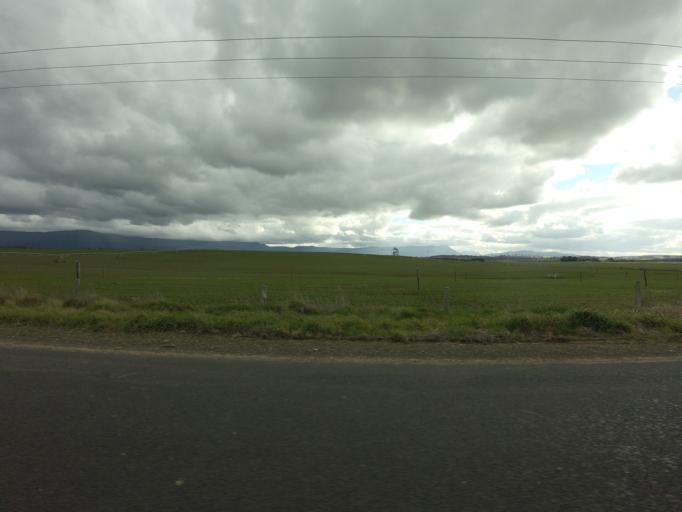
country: AU
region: Tasmania
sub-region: Northern Midlands
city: Longford
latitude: -41.7574
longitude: 147.0826
